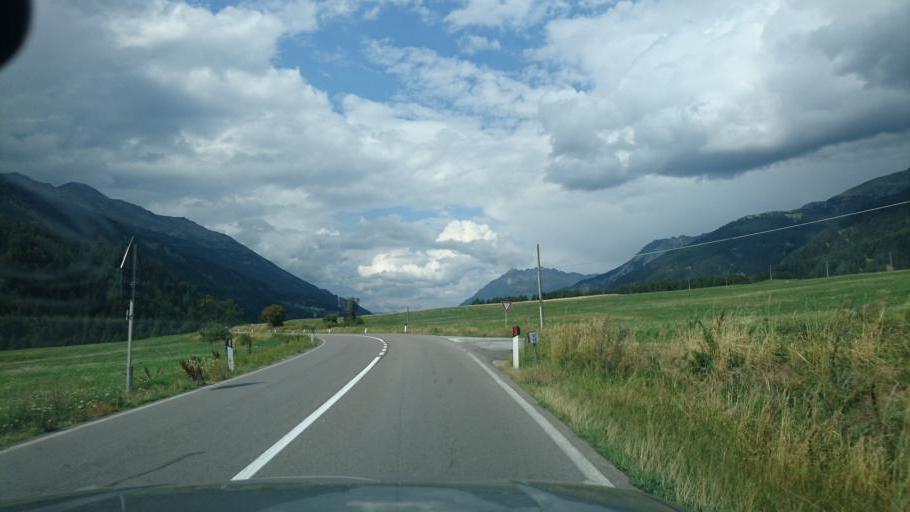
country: IT
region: Trentino-Alto Adige
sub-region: Bolzano
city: Malles Venosta
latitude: 46.7302
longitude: 10.5385
